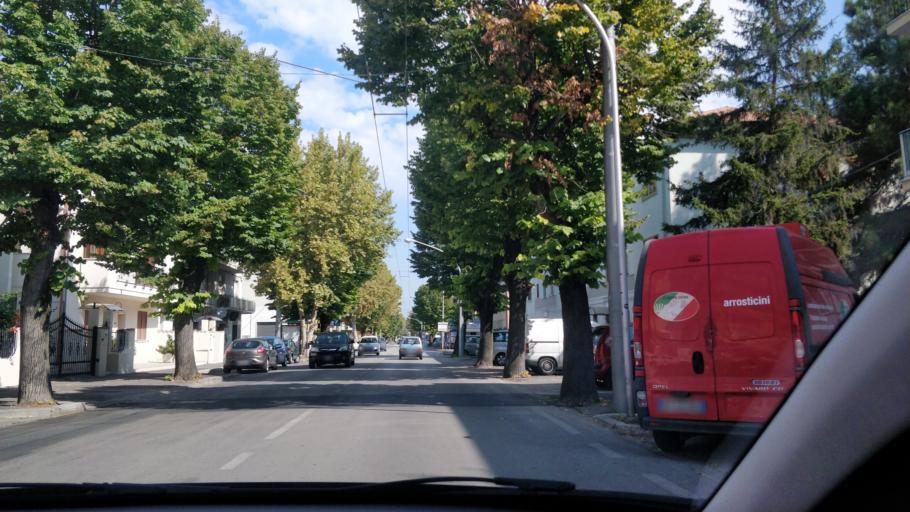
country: IT
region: Abruzzo
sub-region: Provincia di Chieti
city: Chieti
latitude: 42.3674
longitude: 14.1422
